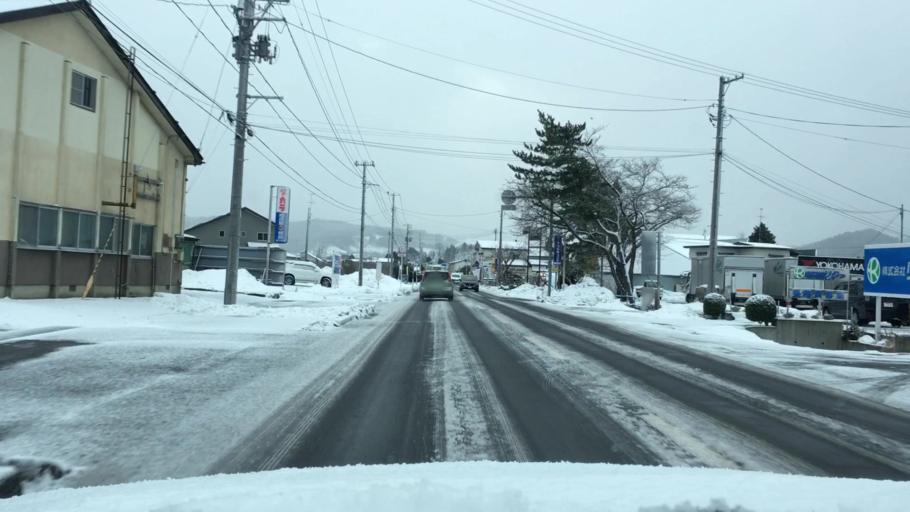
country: JP
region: Aomori
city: Hirosaki
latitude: 40.5593
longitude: 140.5330
